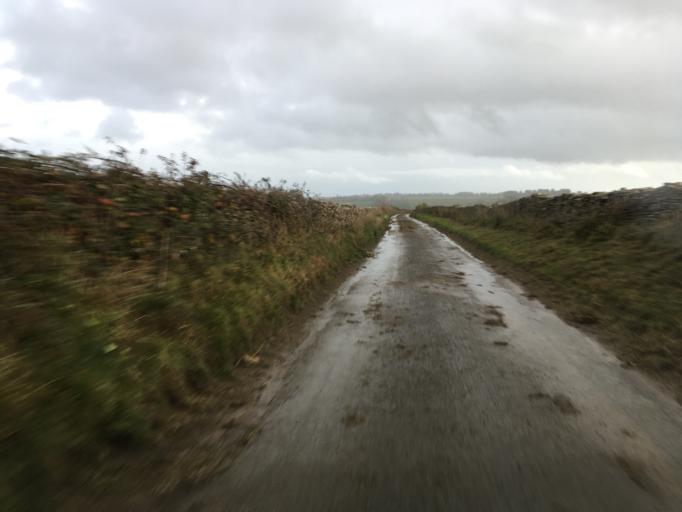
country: GB
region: England
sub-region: South Gloucestershire
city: Cold Ashton
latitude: 51.4681
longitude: -2.3538
